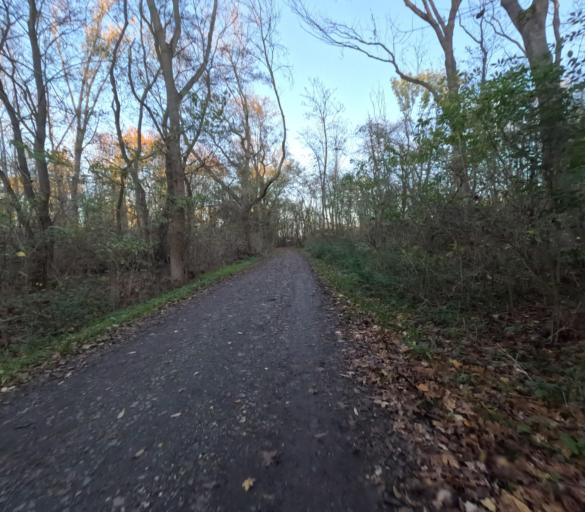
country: DE
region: Saxony
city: Schkeuditz
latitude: 51.3843
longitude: 12.2124
